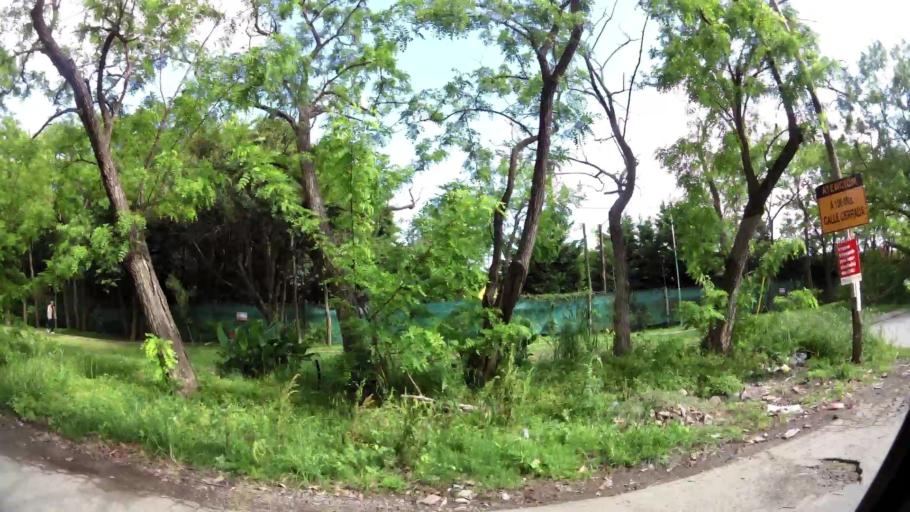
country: AR
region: Buenos Aires
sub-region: Partido de Quilmes
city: Quilmes
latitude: -34.7954
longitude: -58.1580
